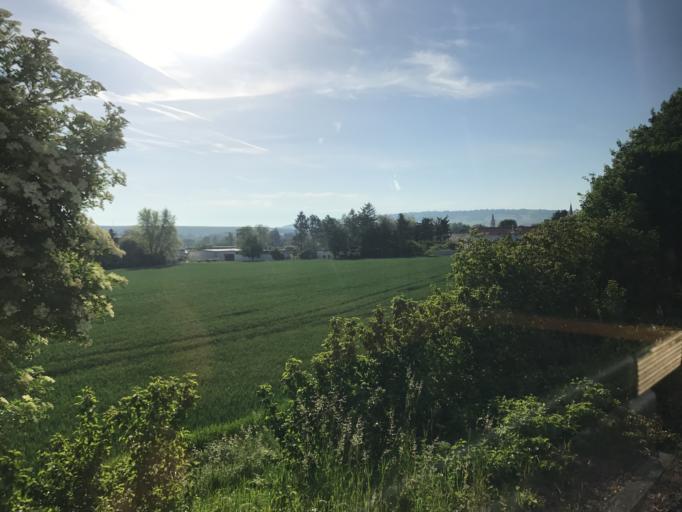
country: DE
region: Rheinland-Pfalz
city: Sprendlingen
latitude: 49.8640
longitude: 7.9753
